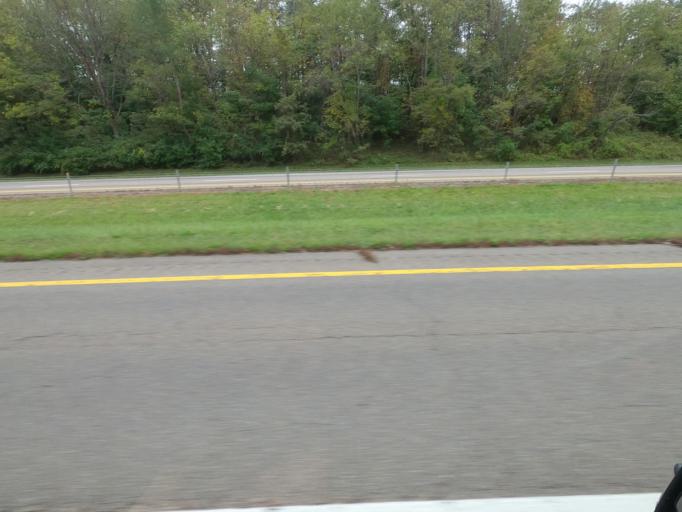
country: US
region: Tennessee
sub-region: Unicoi County
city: Unicoi
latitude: 36.2195
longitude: -82.3439
